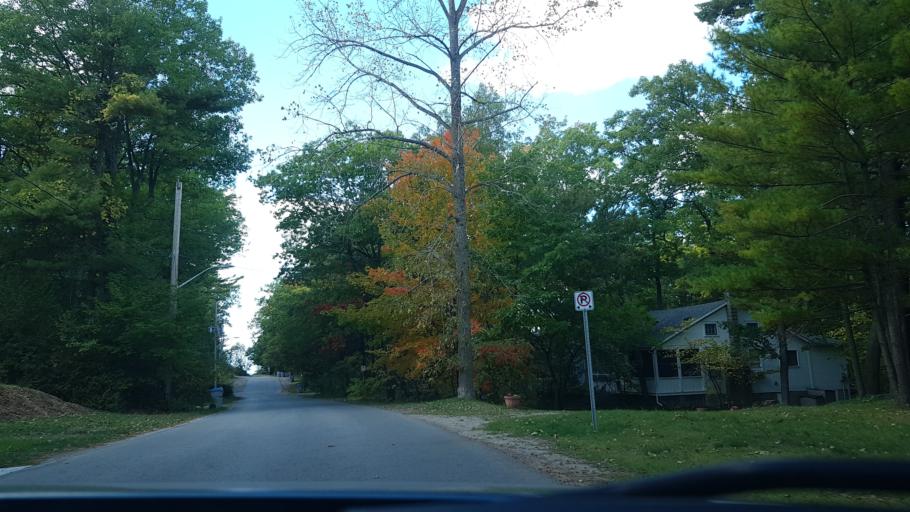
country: CA
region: Ontario
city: Lambton Shores
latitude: 43.3114
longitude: -81.7651
